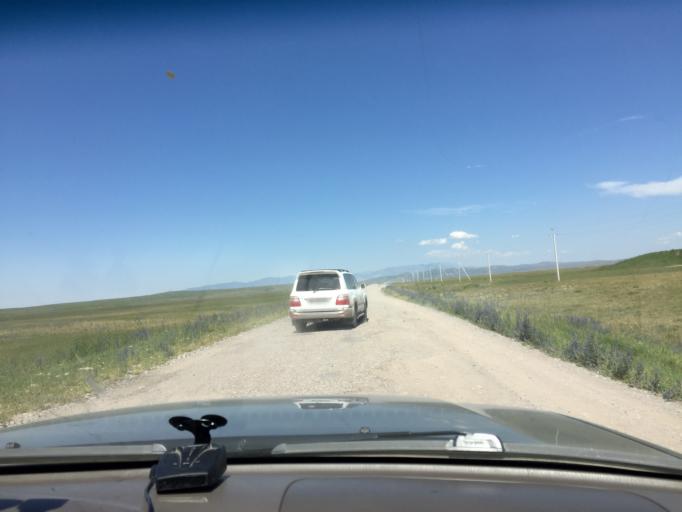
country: KZ
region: Almaty Oblysy
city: Kegen
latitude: 42.7759
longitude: 79.1526
